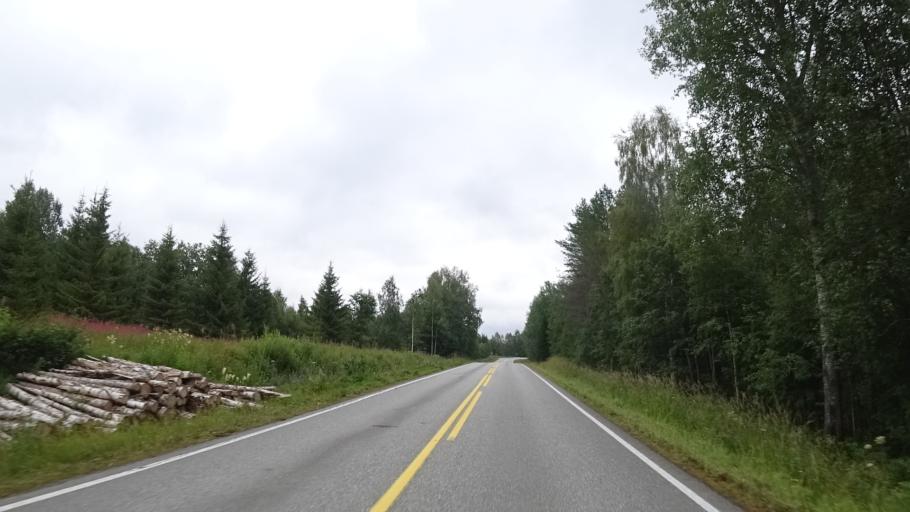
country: FI
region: North Karelia
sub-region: Pielisen Karjala
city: Lieksa
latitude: 63.2804
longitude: 30.6086
